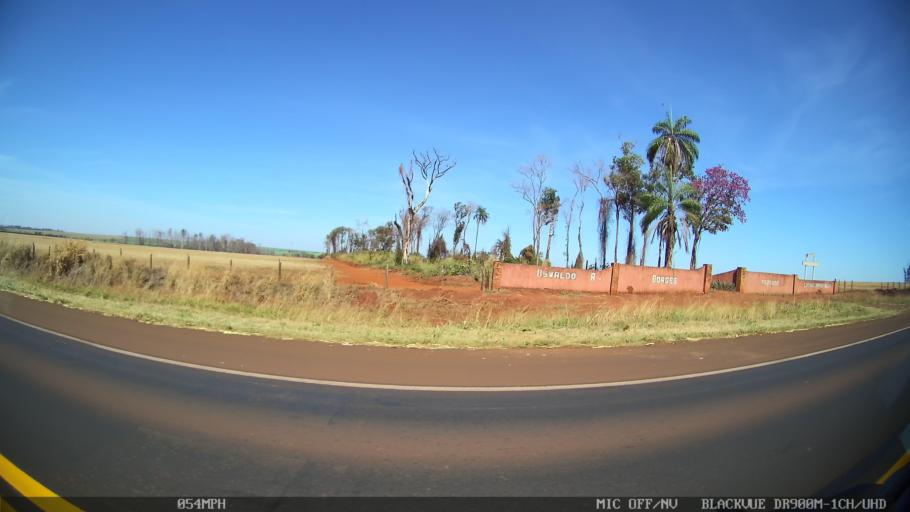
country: BR
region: Sao Paulo
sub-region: Barretos
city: Barretos
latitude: -20.4879
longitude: -48.5168
